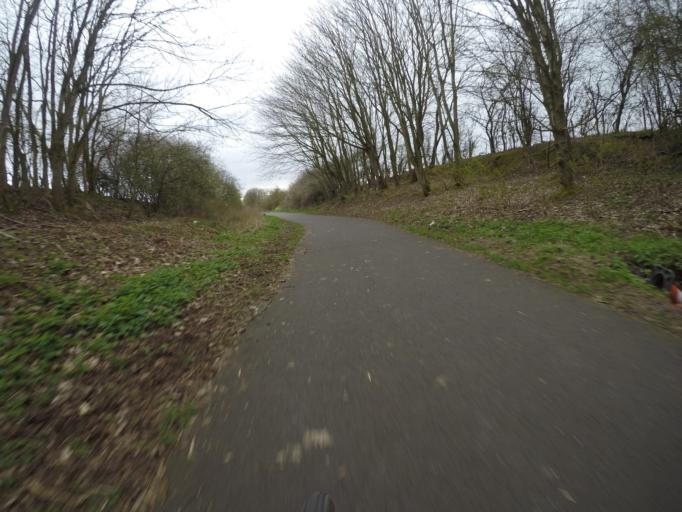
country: GB
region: Scotland
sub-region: North Ayrshire
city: Springside
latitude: 55.6178
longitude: -4.5927
